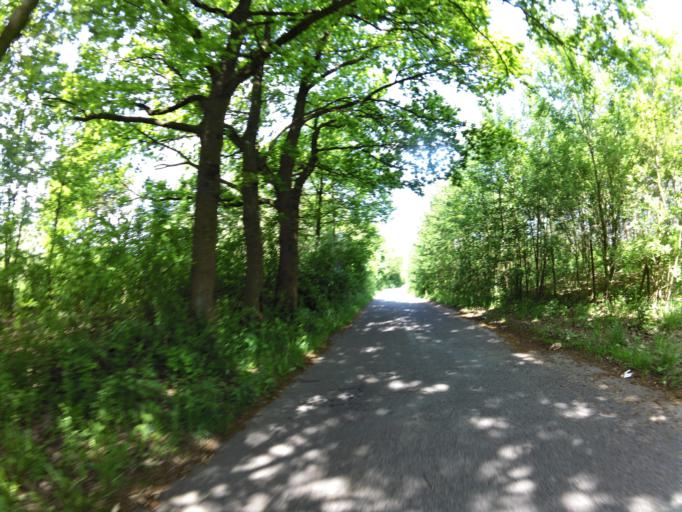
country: NL
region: Limburg
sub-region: Gemeente Heerlen
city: Heerlen
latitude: 50.8606
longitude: 5.9953
